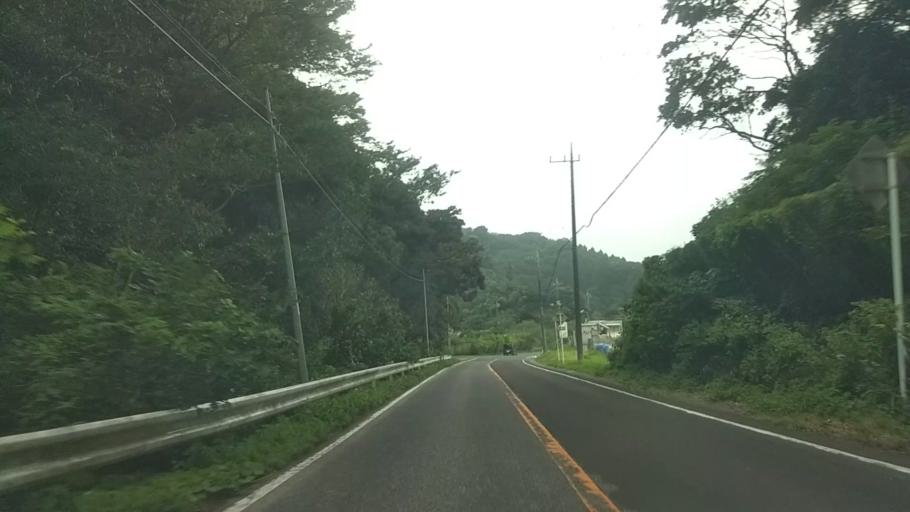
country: JP
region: Chiba
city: Tateyama
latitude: 35.1396
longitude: 139.9061
